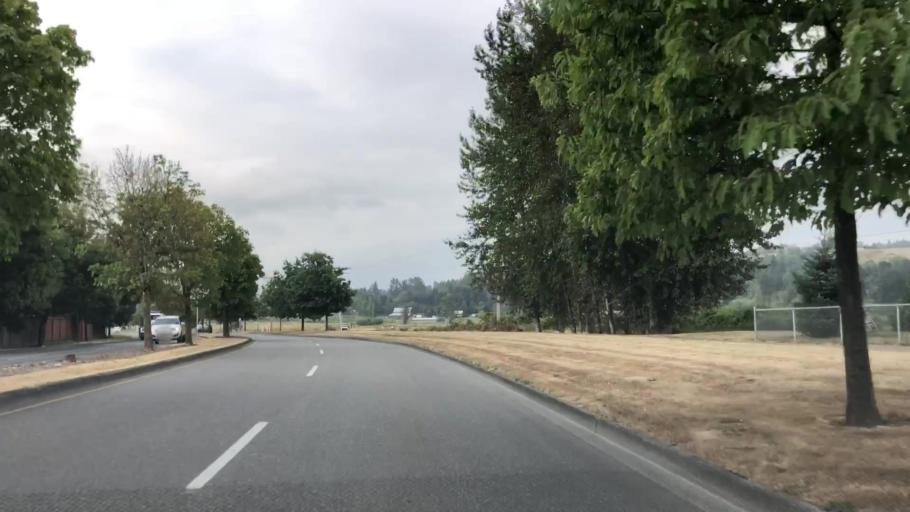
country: US
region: Washington
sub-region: Snohomish County
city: Monroe
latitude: 47.8574
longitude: -122.0118
